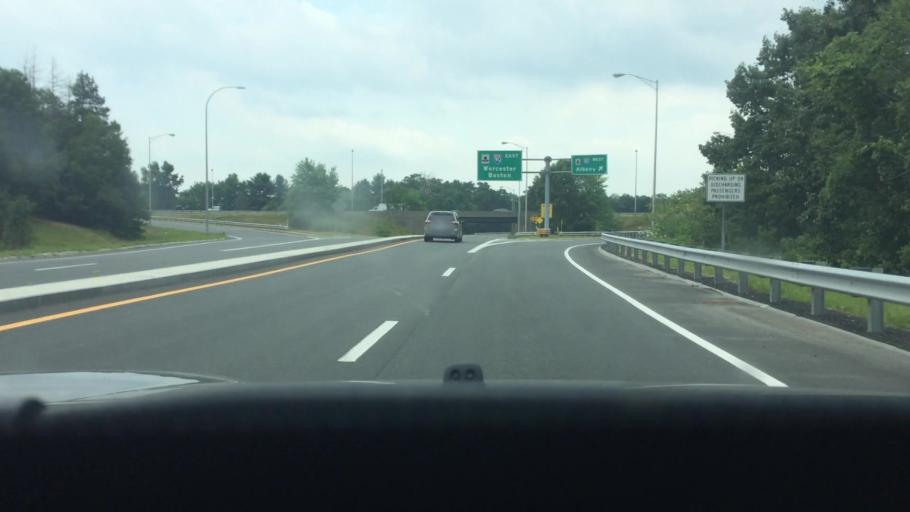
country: US
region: Massachusetts
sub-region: Hampden County
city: North Chicopee
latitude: 42.1715
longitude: -72.5809
